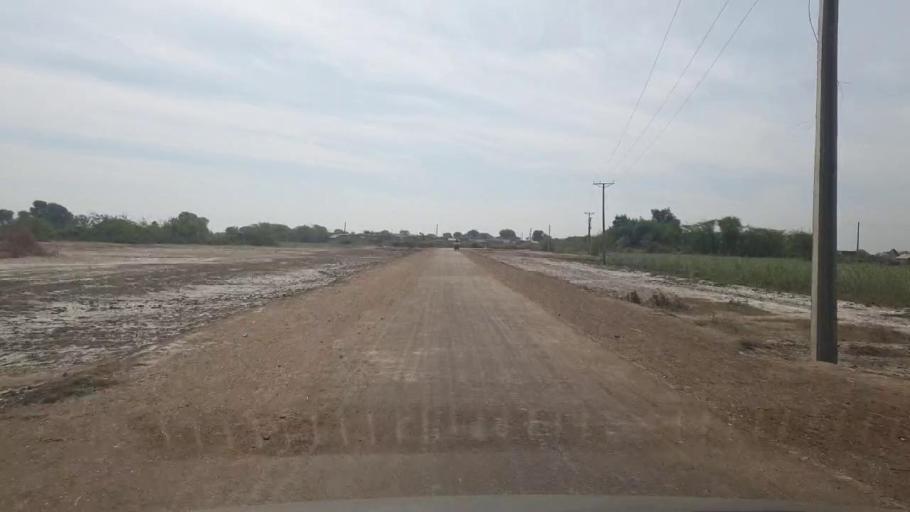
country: PK
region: Sindh
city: Umarkot
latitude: 25.3254
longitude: 69.5926
